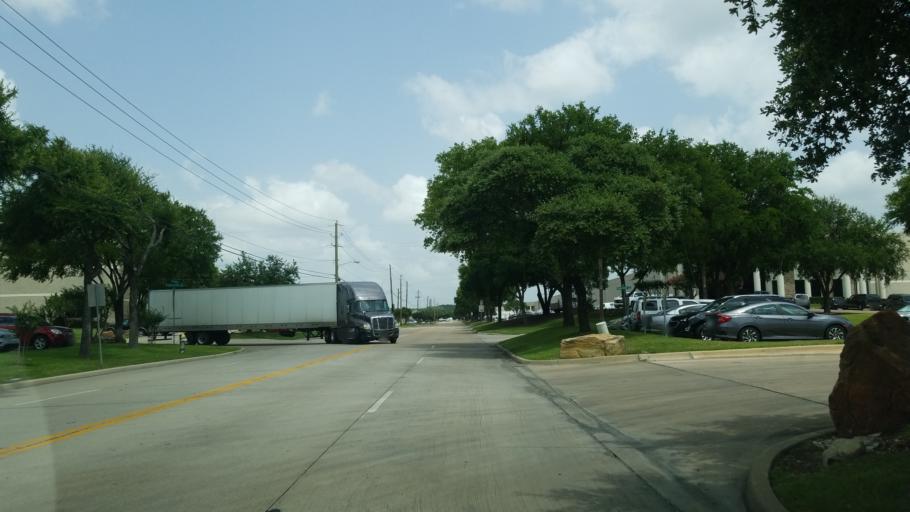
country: US
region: Texas
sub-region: Dallas County
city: Cockrell Hill
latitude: 32.7710
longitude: -96.8897
